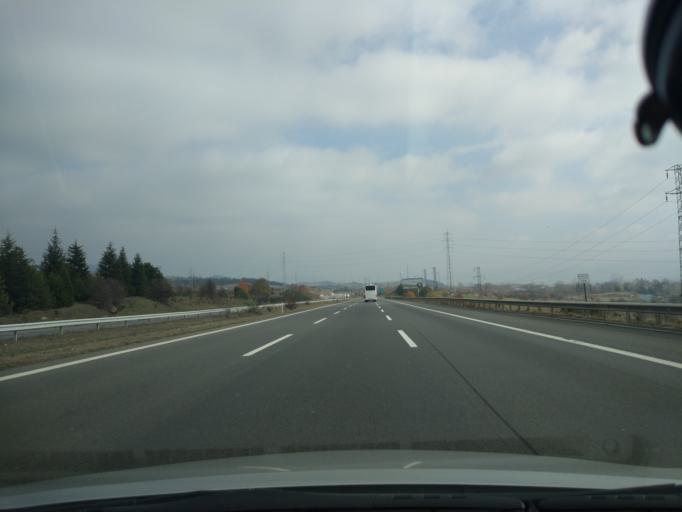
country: TR
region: Bolu
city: Bolu
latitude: 40.7645
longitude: 31.6198
